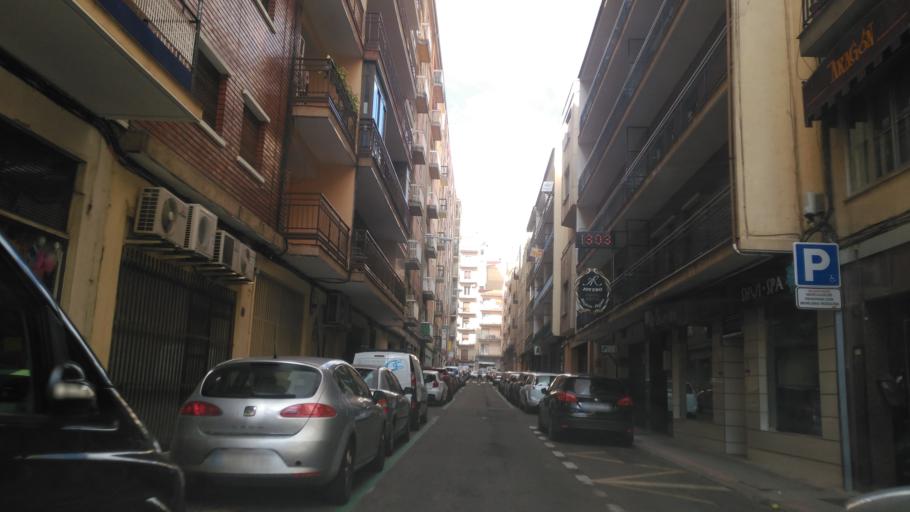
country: ES
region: Castille and Leon
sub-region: Provincia de Salamanca
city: Salamanca
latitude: 40.9716
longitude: -5.6582
